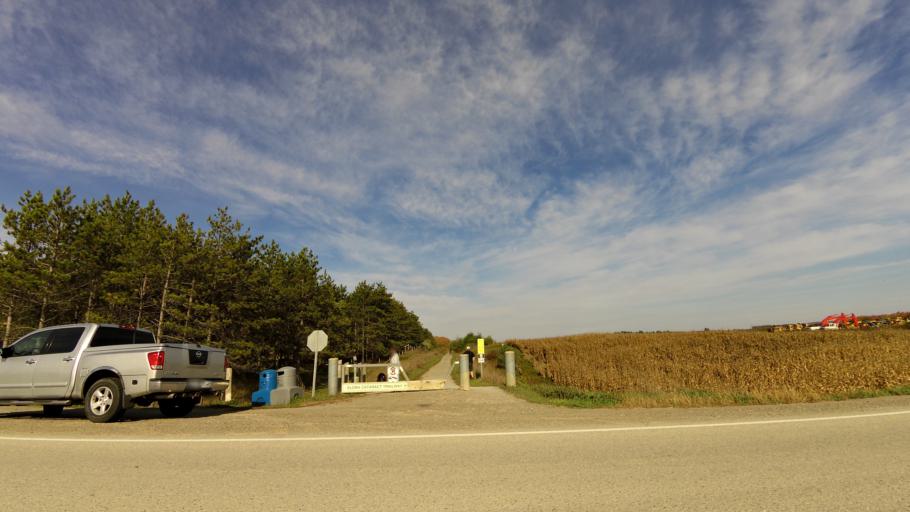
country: CA
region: Ontario
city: Orangeville
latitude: 43.7931
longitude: -80.0474
